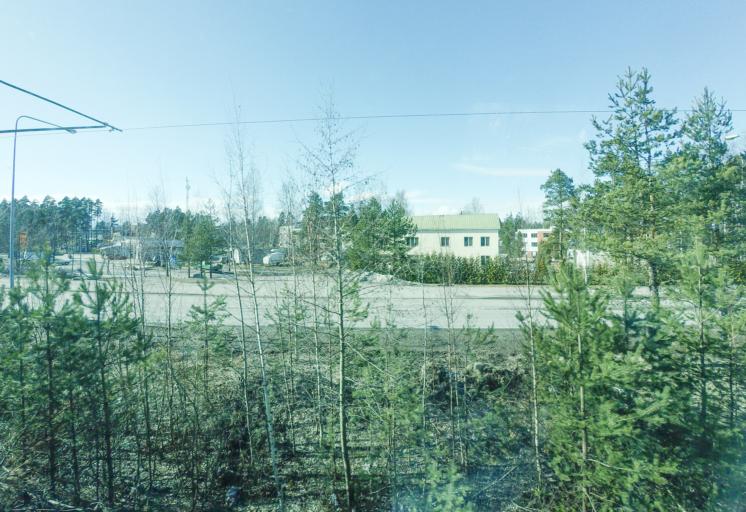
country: FI
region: South Karelia
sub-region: Lappeenranta
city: Lappeenranta
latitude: 61.0716
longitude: 28.2676
